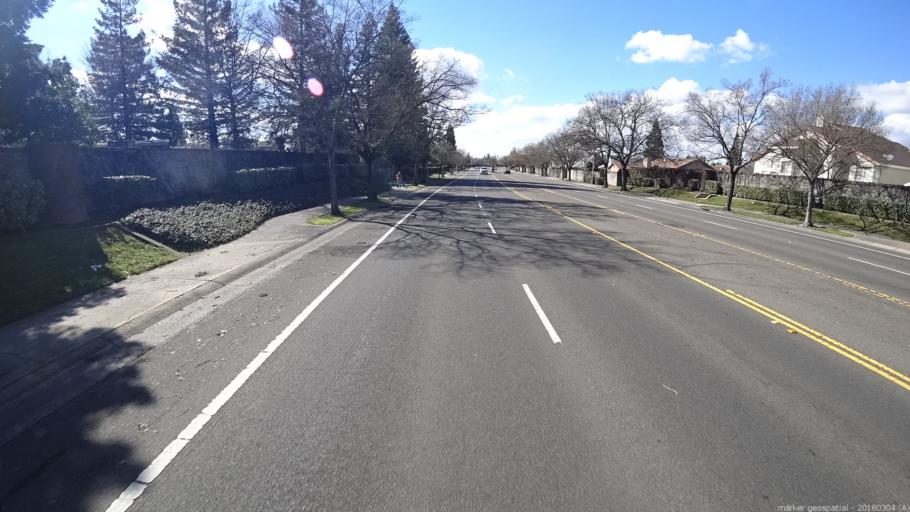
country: US
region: California
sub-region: Sacramento County
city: Vineyard
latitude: 38.4646
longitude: -121.3621
